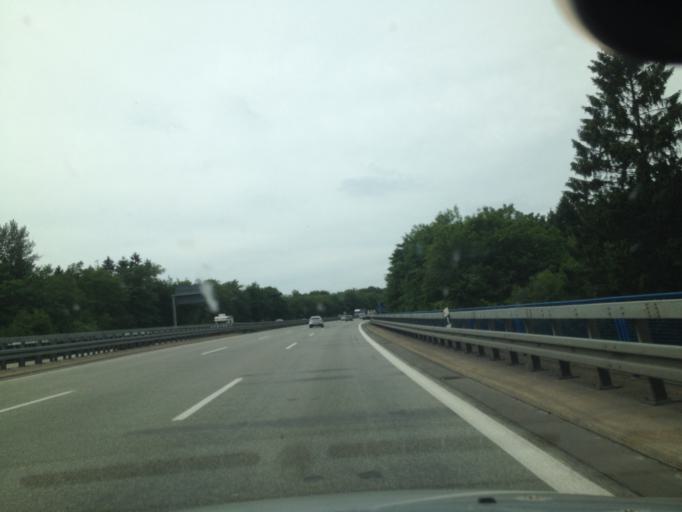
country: DE
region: North Rhine-Westphalia
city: Meinerzhagen
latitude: 51.1111
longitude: 7.6694
